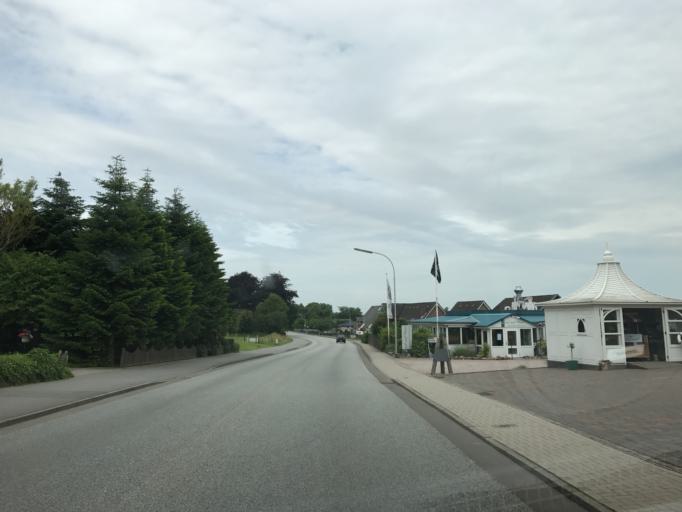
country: DE
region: Schleswig-Holstein
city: Nindorf
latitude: 54.0869
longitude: 9.1131
